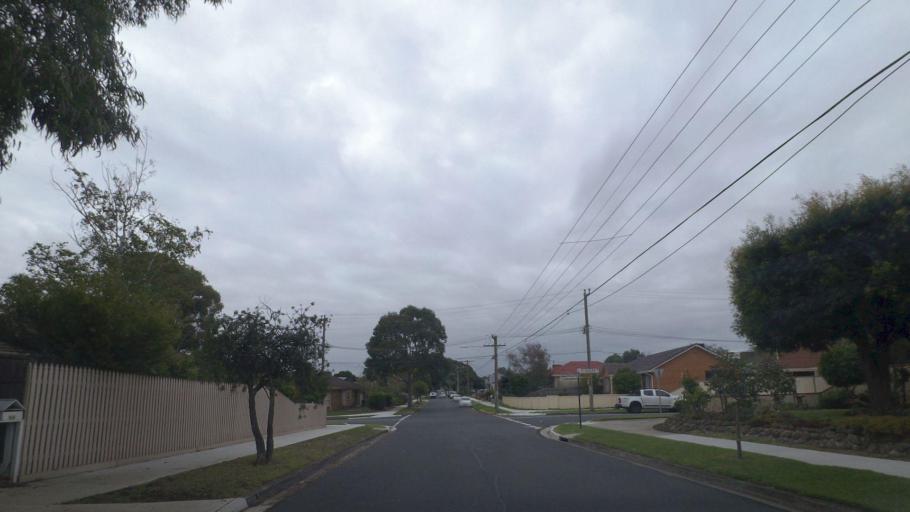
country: AU
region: Victoria
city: Forest Hill
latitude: -37.8349
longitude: 145.1848
